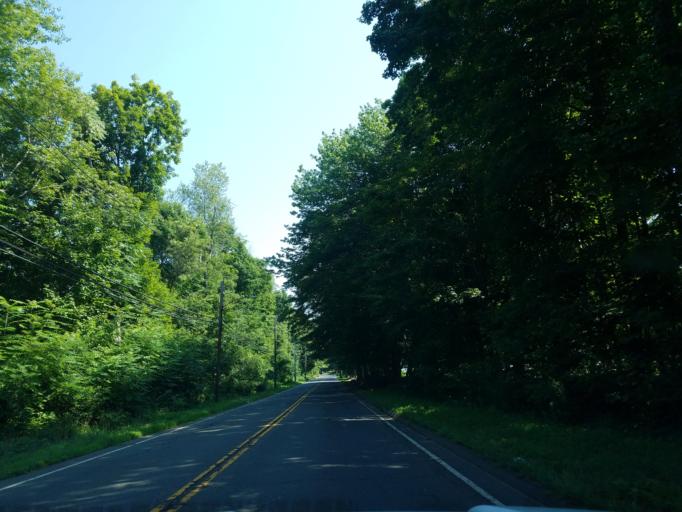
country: US
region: Connecticut
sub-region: New Haven County
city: City of Milford (balance)
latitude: 41.2507
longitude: -73.0520
